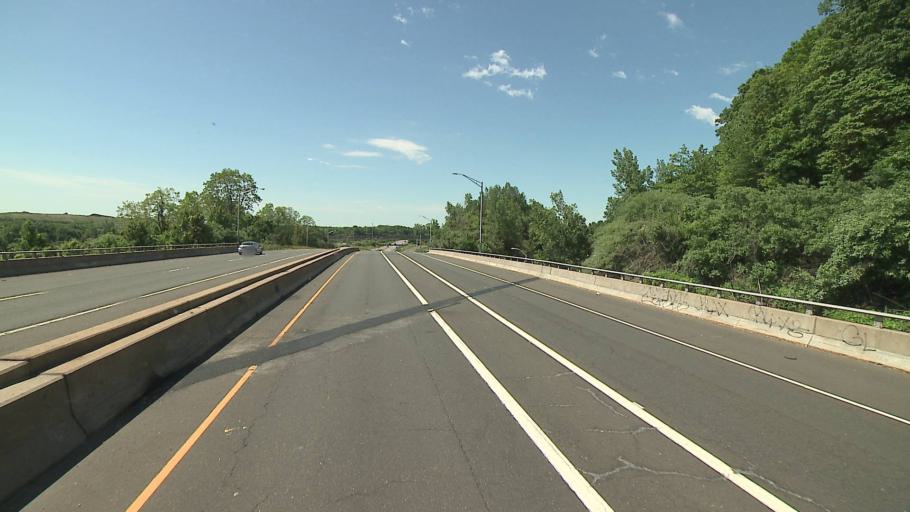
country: US
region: Connecticut
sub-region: Hartford County
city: East Hartford
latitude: 41.7840
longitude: -72.5693
